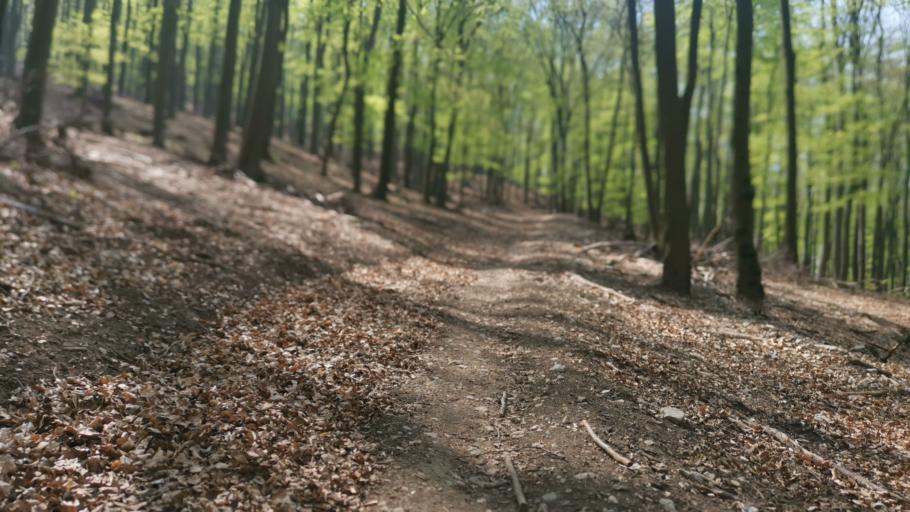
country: SK
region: Trnavsky
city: Smolenice
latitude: 48.5297
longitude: 17.4156
